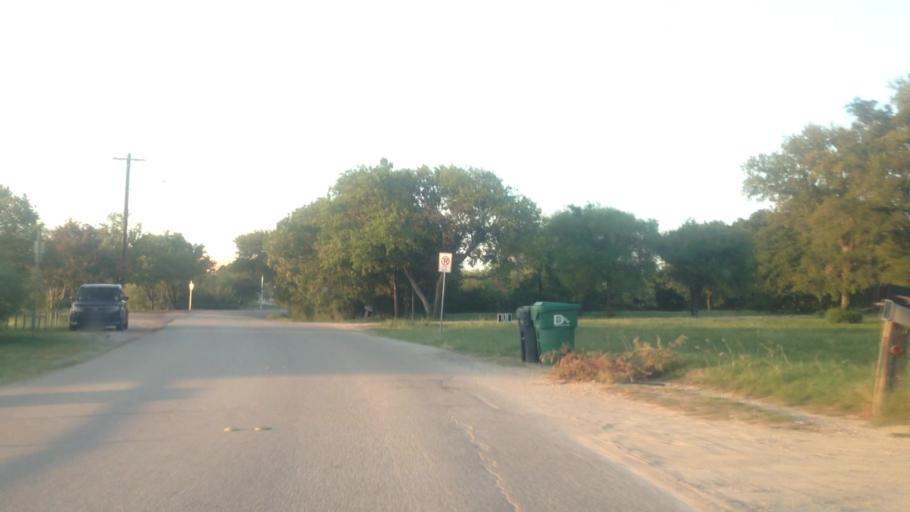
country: US
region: Texas
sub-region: Denton County
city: Denton
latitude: 33.2022
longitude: -97.1542
